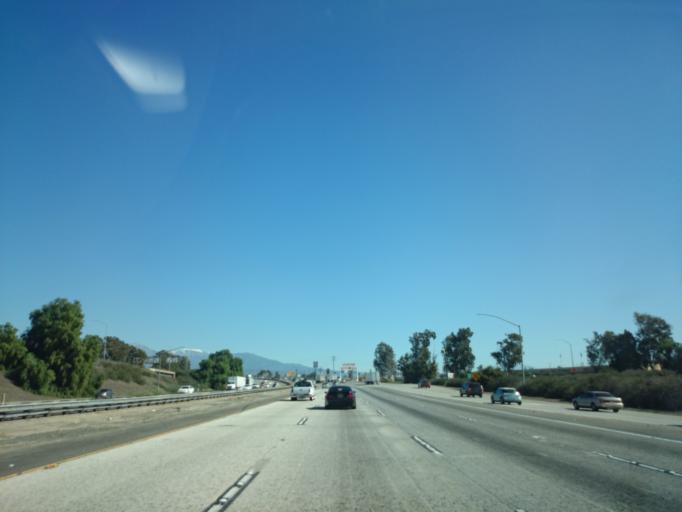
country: US
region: California
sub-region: San Bernardino County
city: Colton
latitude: 34.0637
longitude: -117.2936
